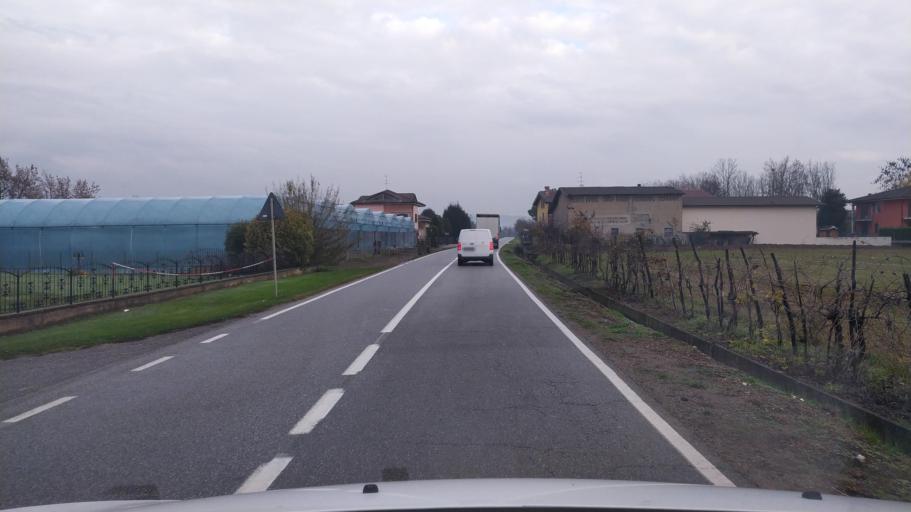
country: IT
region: Lombardy
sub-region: Provincia di Brescia
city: Pontoglio
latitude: 45.5532
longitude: 9.8577
